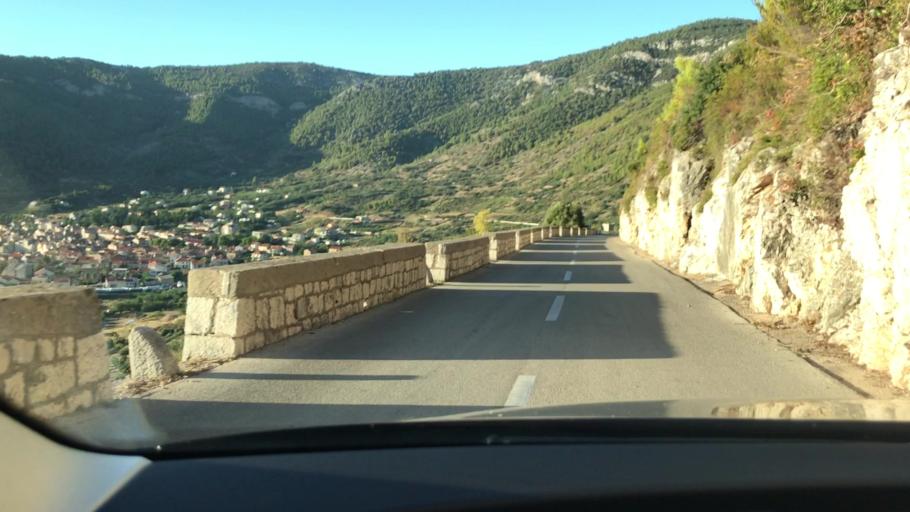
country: HR
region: Splitsko-Dalmatinska
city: Komiza
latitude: 43.0356
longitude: 16.0948
